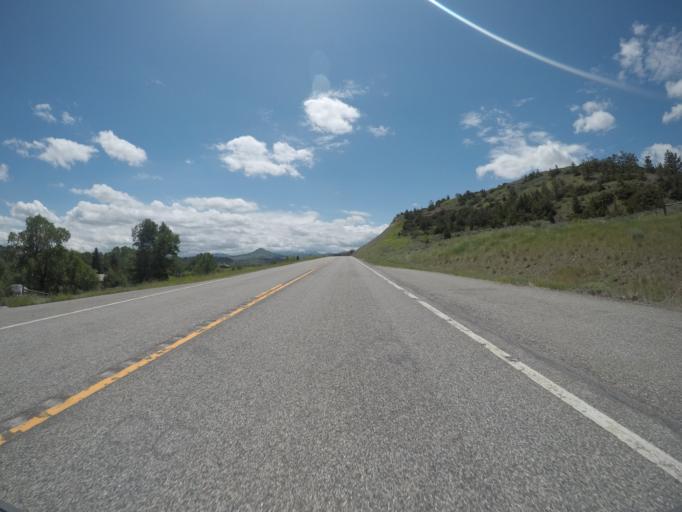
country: US
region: Montana
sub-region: Sweet Grass County
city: Big Timber
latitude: 45.7408
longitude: -109.9971
